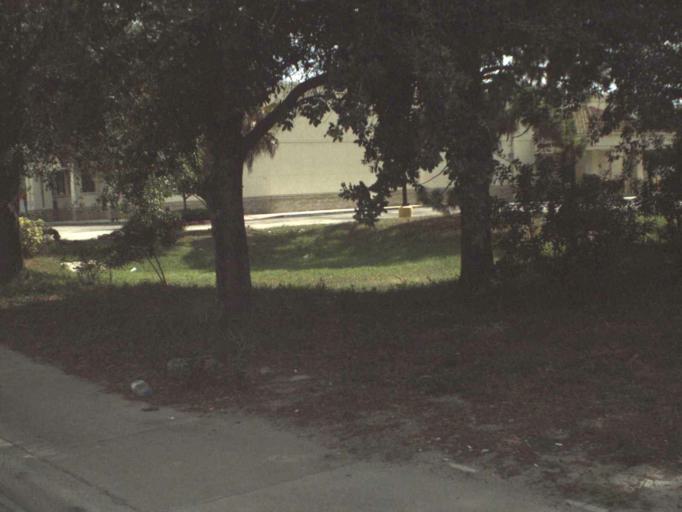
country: US
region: Florida
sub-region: Saint Lucie County
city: Fort Pierce
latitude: 27.4463
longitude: -80.3498
